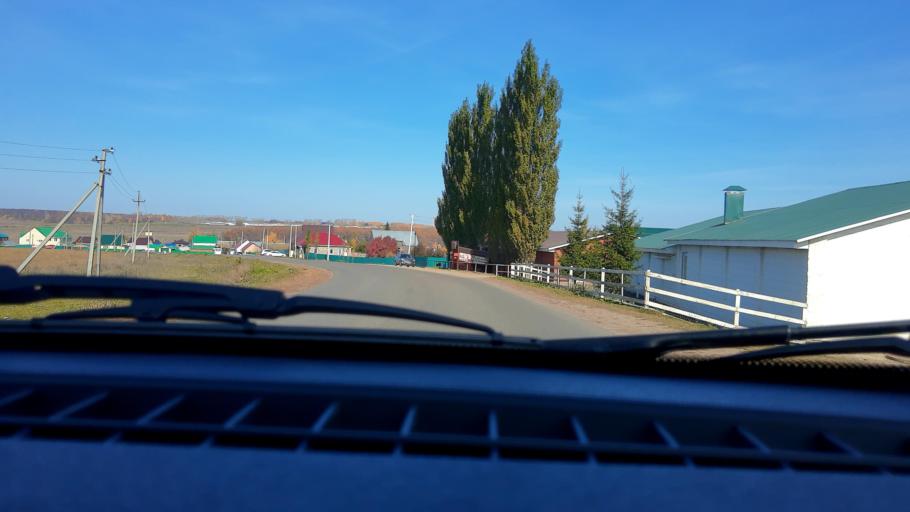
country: RU
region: Bashkortostan
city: Mikhaylovka
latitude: 54.8138
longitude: 55.7891
